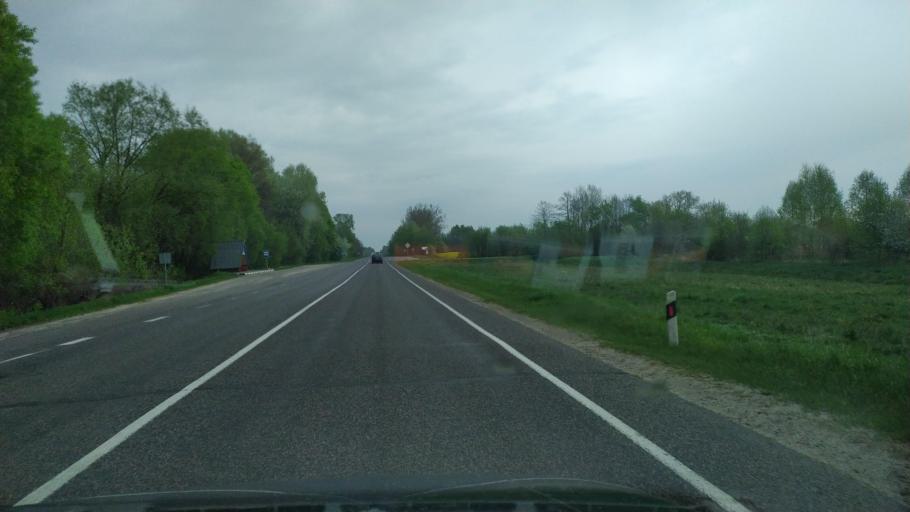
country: BY
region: Brest
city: Horad Kobryn
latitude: 52.2906
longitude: 24.5004
